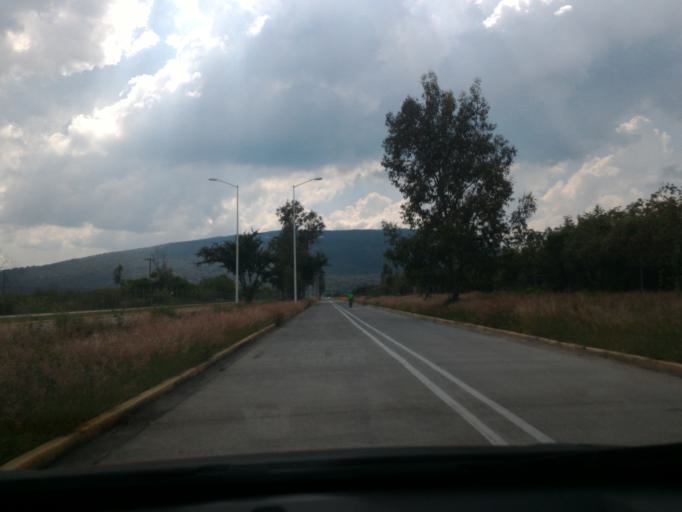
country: MX
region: Jalisco
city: Nuevo Mexico
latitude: 20.6935
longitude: -103.4638
